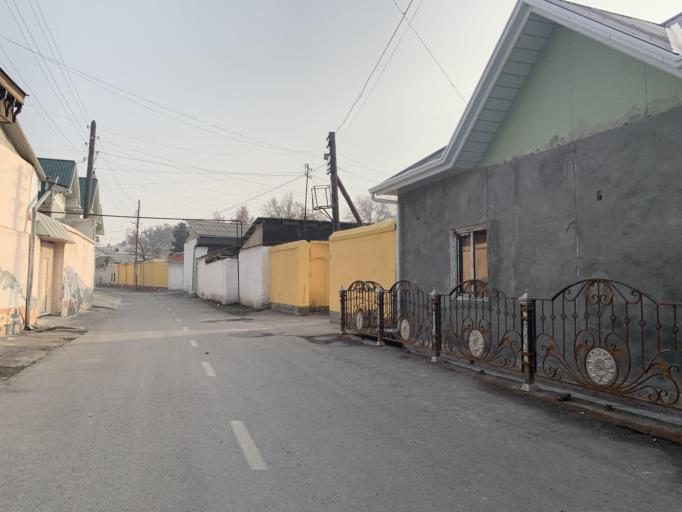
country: UZ
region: Fergana
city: Qo`qon
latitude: 40.5376
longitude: 70.9286
